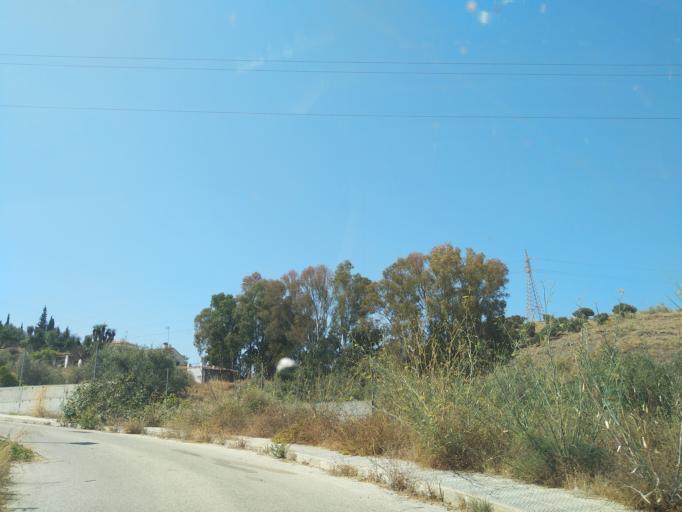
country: ES
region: Andalusia
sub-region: Provincia de Malaga
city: Valdes
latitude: 36.7221
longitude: -4.1996
